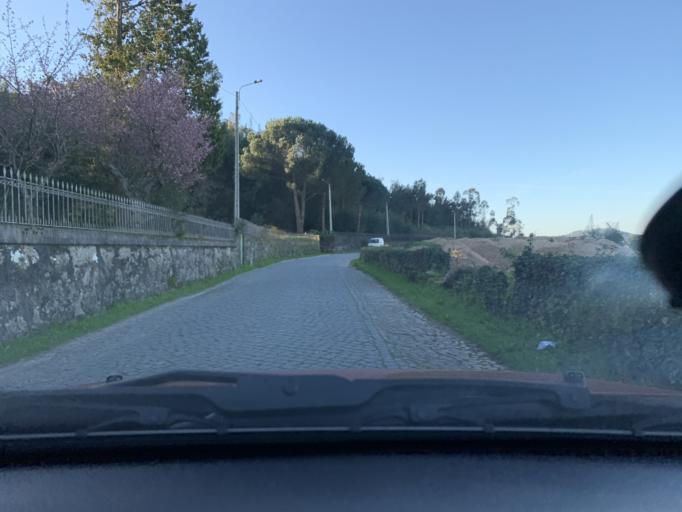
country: PT
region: Braga
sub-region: Vila Nova de Famalicao
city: Vila Nova de Famalicao
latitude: 41.4090
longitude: -8.5069
